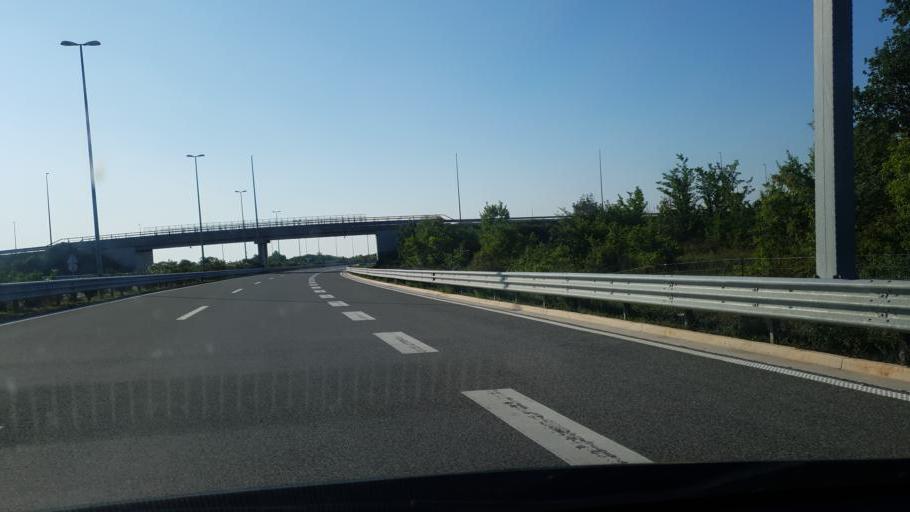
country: HR
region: Istarska
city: Vodnjan
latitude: 44.9858
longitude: 13.8480
